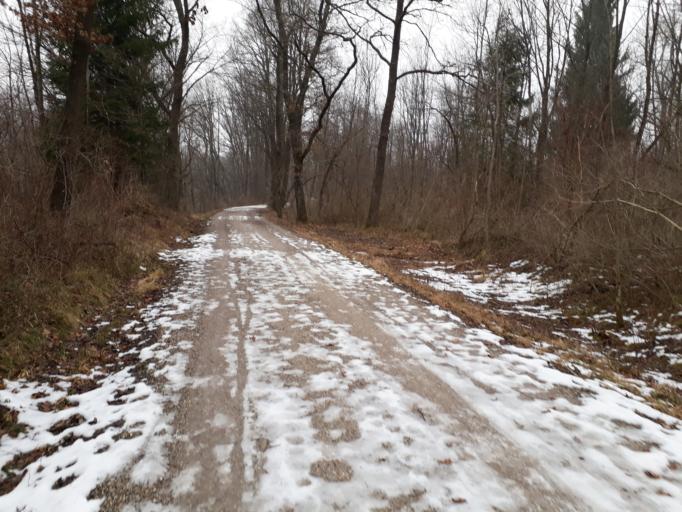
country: DE
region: Bavaria
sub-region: Upper Bavaria
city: Unterfoehring
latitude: 48.2168
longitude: 11.6518
